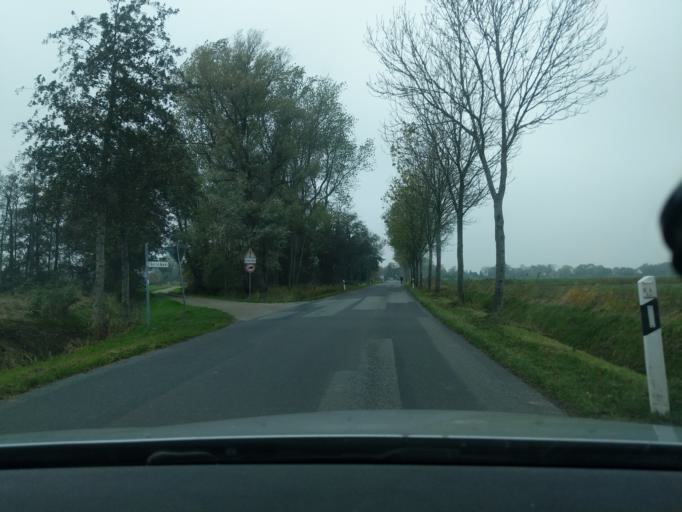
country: DE
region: Lower Saxony
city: Nordleda
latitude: 53.8272
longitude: 8.7860
